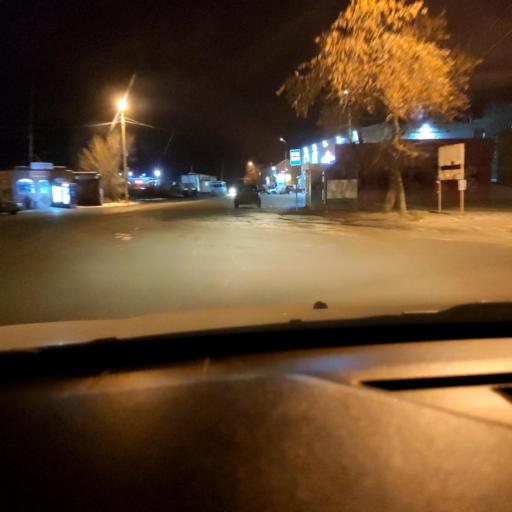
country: RU
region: Samara
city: Smyshlyayevka
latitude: 53.2525
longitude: 50.4787
